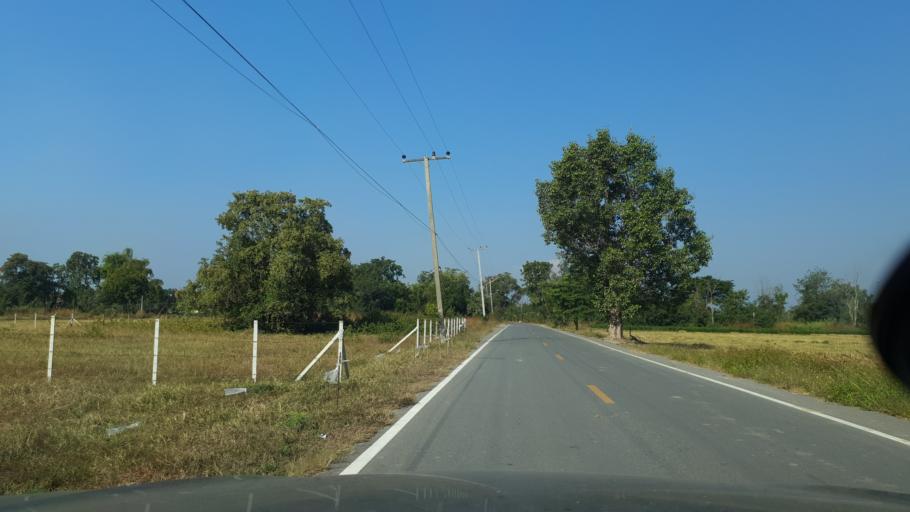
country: TH
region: Lamphun
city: Ban Thi
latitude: 18.6845
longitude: 99.1165
